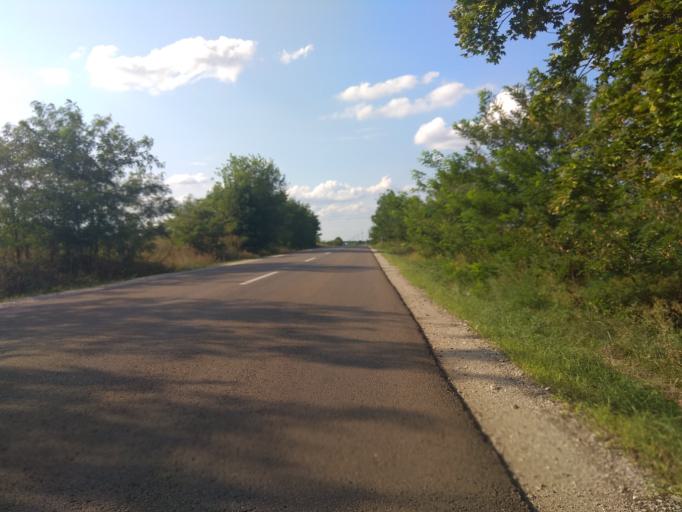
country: HU
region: Borsod-Abauj-Zemplen
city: Emod
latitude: 47.9161
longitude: 20.8824
